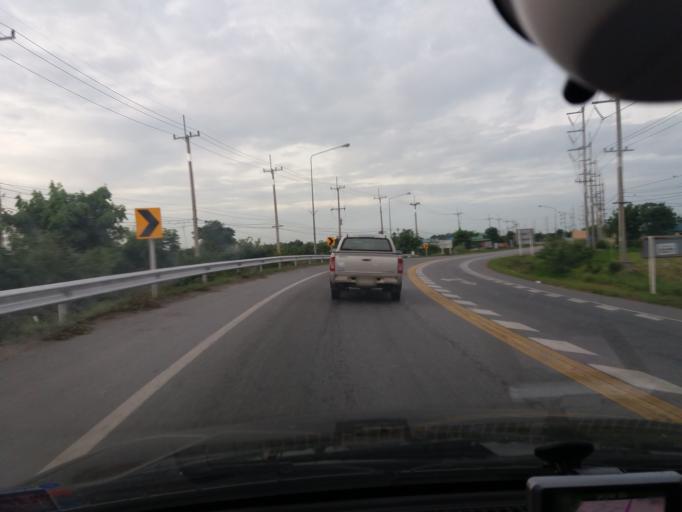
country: TH
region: Suphan Buri
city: U Thong
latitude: 14.5115
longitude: 99.9161
